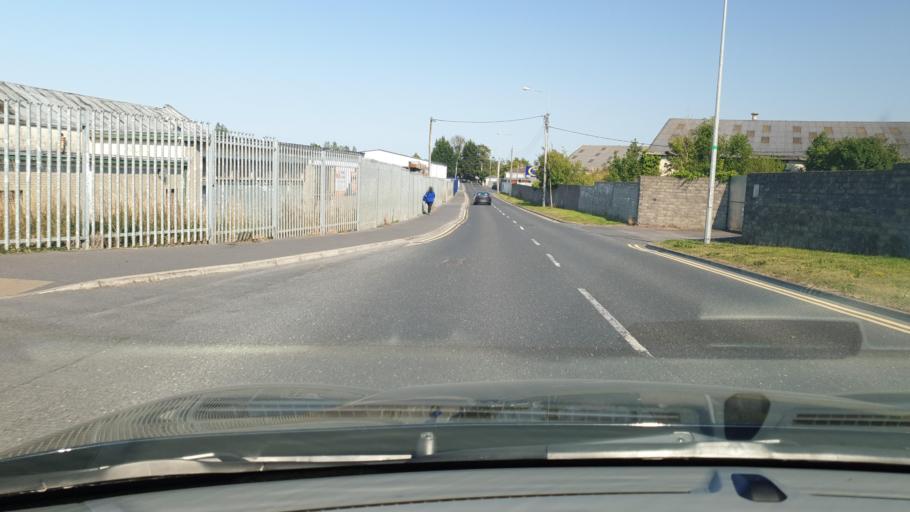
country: IE
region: Leinster
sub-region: An Mhi
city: Navan
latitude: 53.6475
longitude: -6.6905
